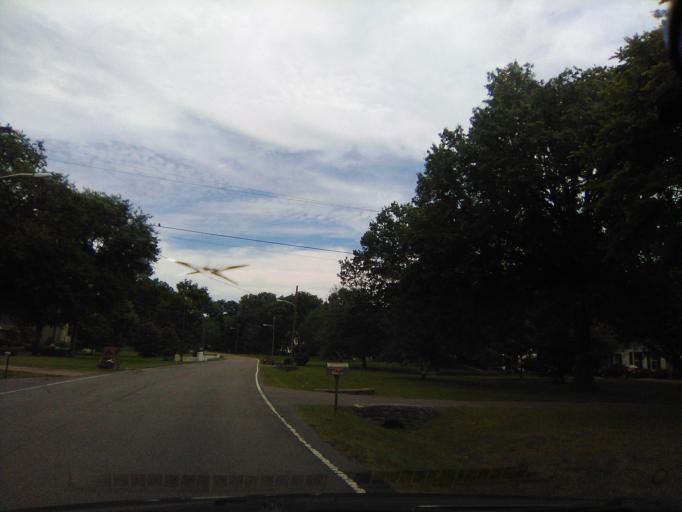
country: US
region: Tennessee
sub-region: Davidson County
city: Belle Meade
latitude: 36.0995
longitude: -86.8774
